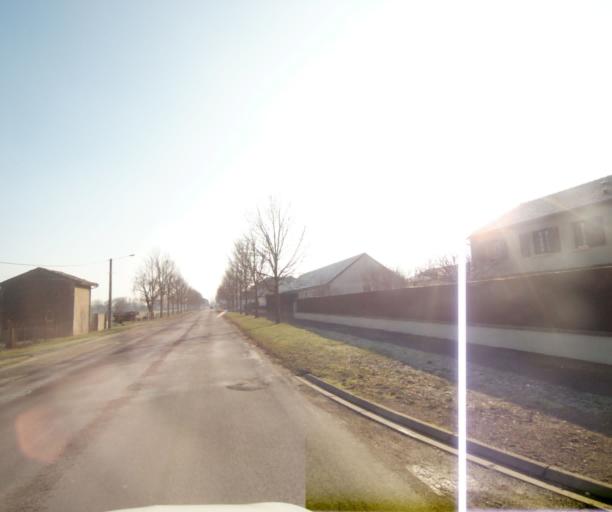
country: FR
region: Champagne-Ardenne
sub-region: Departement de la Haute-Marne
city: Montier-en-Der
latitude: 48.4755
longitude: 4.7812
